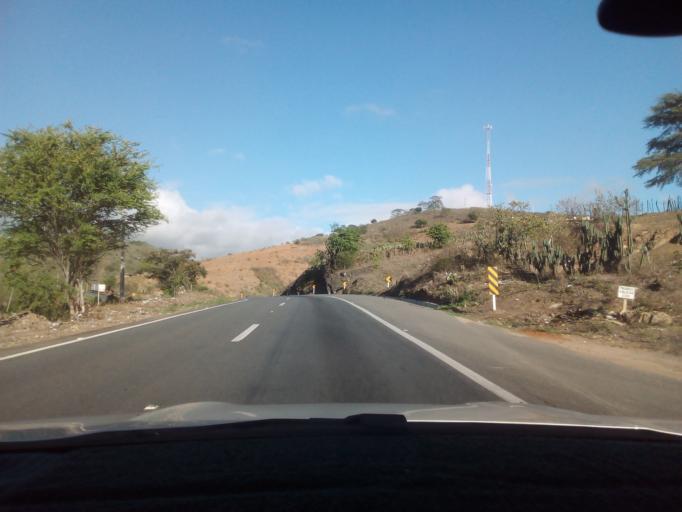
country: BR
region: Paraiba
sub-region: Inga
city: Inga
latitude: -7.2473
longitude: -35.6692
